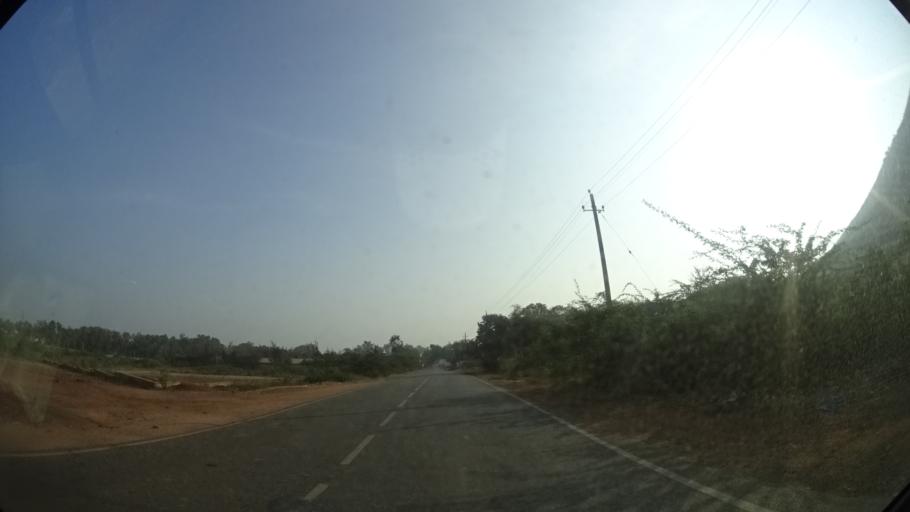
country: IN
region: Karnataka
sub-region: Bellary
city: Hospet
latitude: 15.2579
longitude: 76.3760
